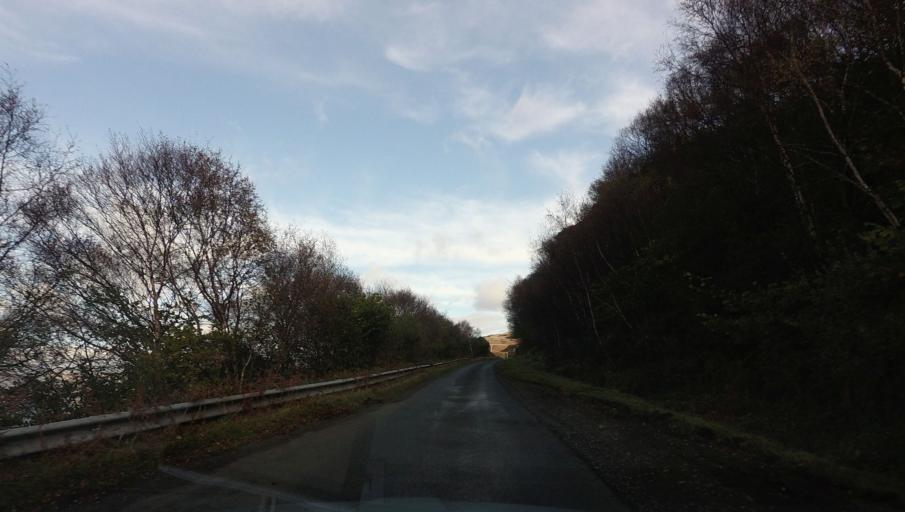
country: GB
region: Scotland
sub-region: Argyll and Bute
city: Isle Of Mull
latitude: 56.3365
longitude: -6.1552
